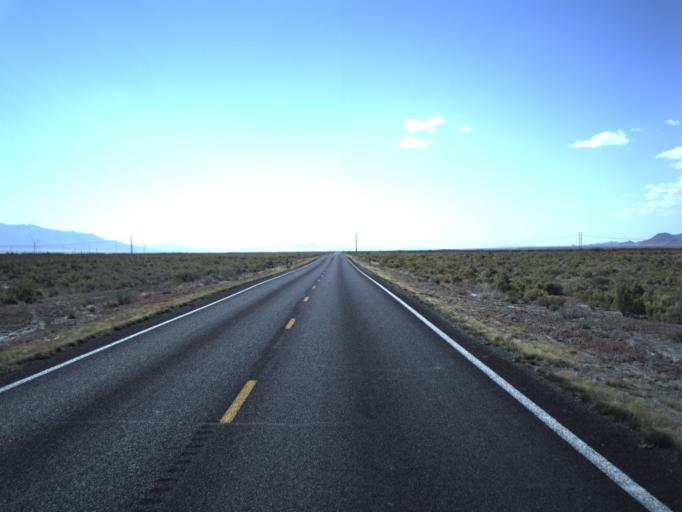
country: US
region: Utah
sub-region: Beaver County
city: Milford
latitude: 38.5847
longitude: -112.9888
